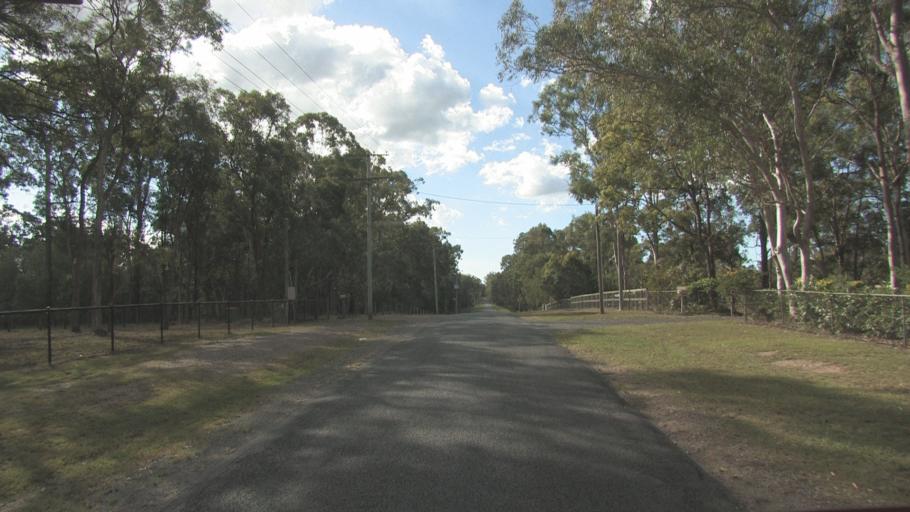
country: AU
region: Queensland
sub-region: Gold Coast
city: Yatala
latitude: -27.6654
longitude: 153.2407
